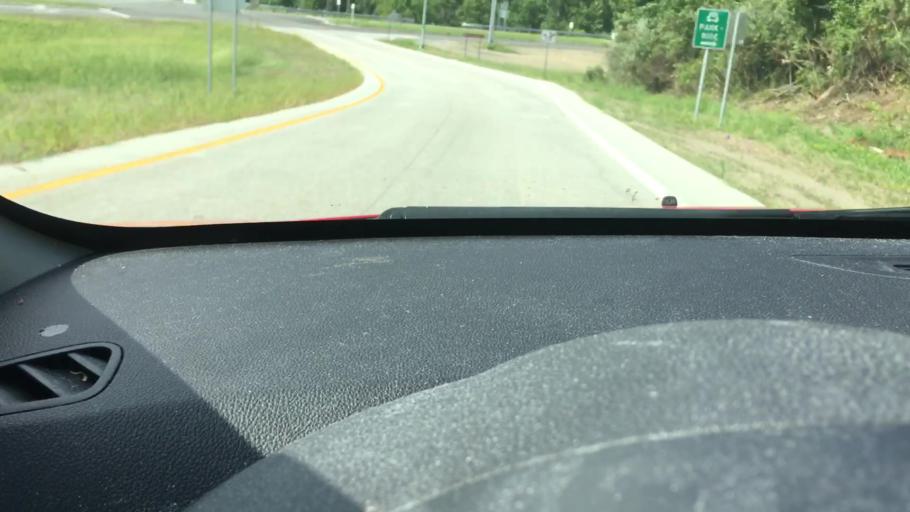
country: US
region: Ohio
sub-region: Athens County
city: The Plains
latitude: 39.3618
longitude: -82.1053
